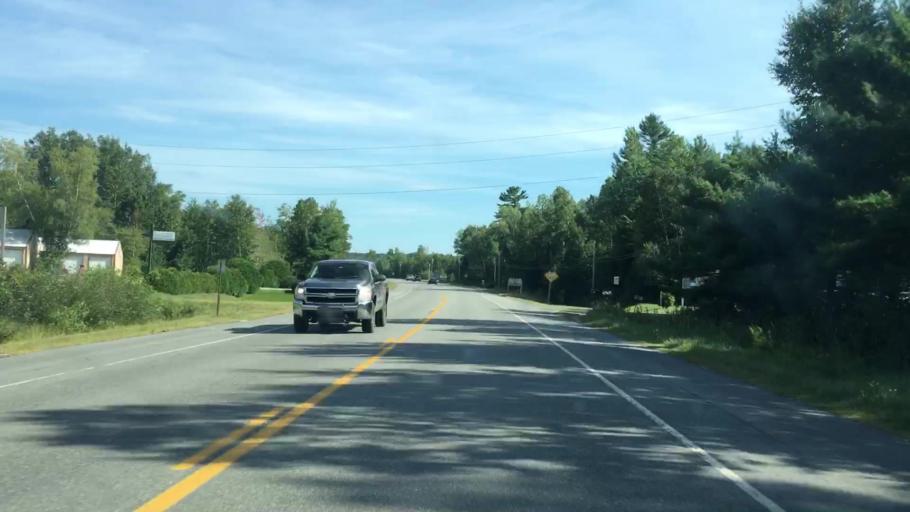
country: US
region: Maine
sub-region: Penobscot County
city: Lincoln
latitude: 45.3603
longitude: -68.5453
